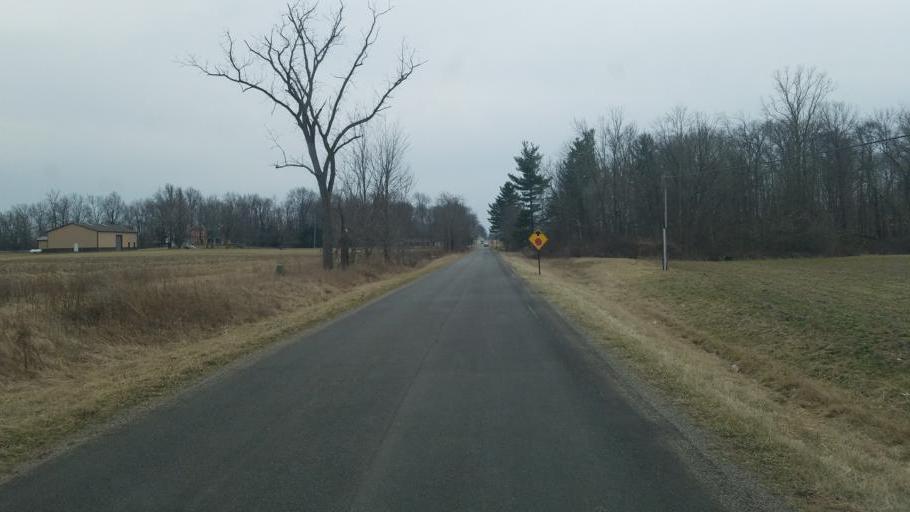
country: US
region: Ohio
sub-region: Crawford County
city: Galion
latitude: 40.6864
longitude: -82.7936
